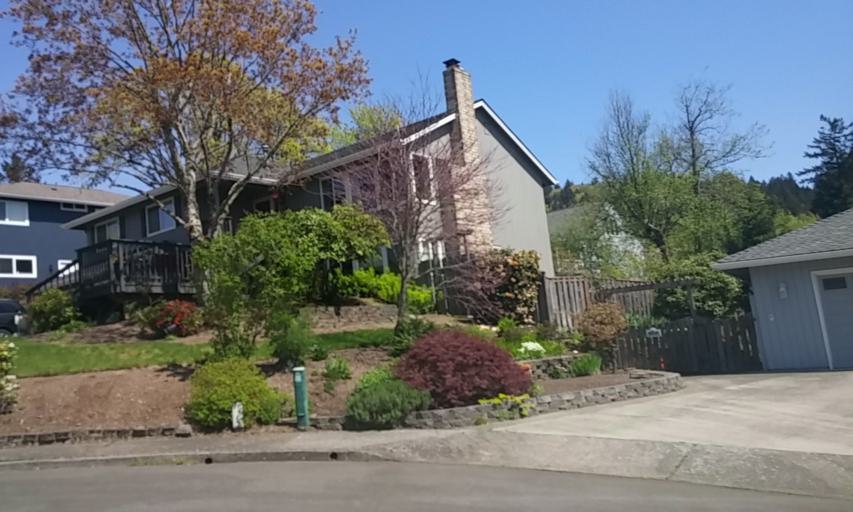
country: US
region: Oregon
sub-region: Washington County
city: West Haven
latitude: 45.5231
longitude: -122.7663
